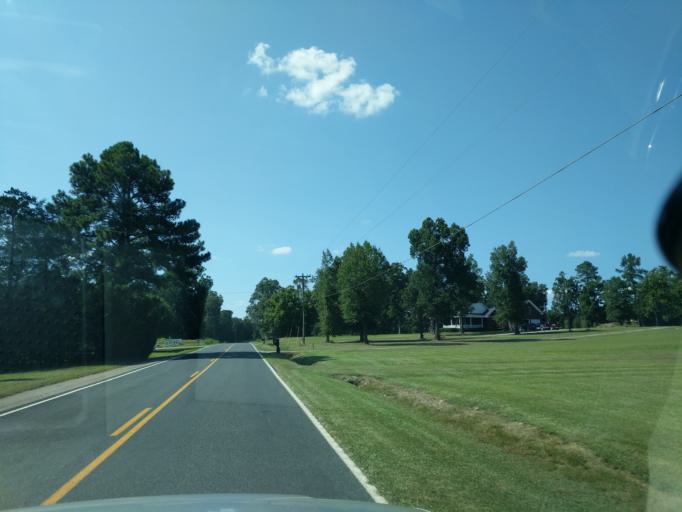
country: US
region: South Carolina
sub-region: Lexington County
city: Leesville
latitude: 34.0249
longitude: -81.5289
